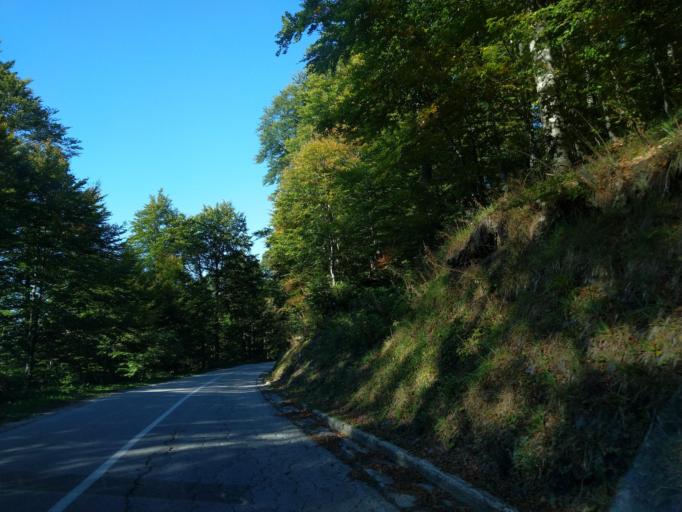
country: RS
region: Central Serbia
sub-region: Moravicki Okrug
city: Ivanjica
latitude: 43.4420
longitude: 20.2714
